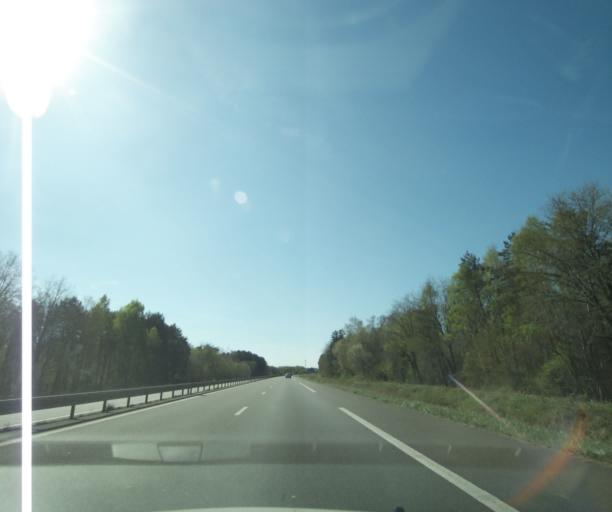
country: FR
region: Centre
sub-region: Departement du Loir-et-Cher
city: Theillay
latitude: 47.3220
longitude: 2.0495
